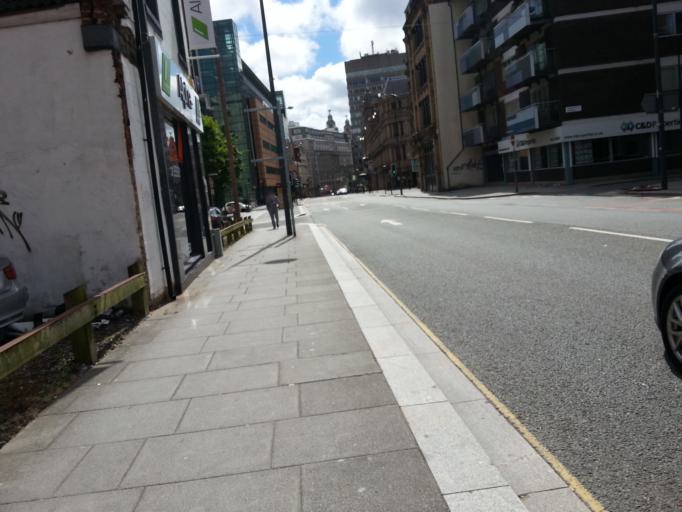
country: GB
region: England
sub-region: Liverpool
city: Liverpool
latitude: 53.4098
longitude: -2.9896
